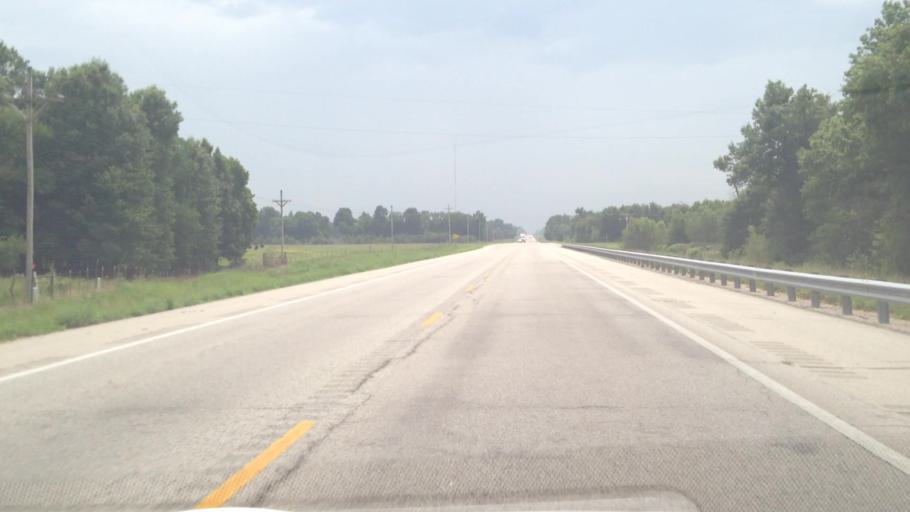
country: US
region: Kansas
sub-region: Cherokee County
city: Galena
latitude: 37.1365
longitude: -94.7043
